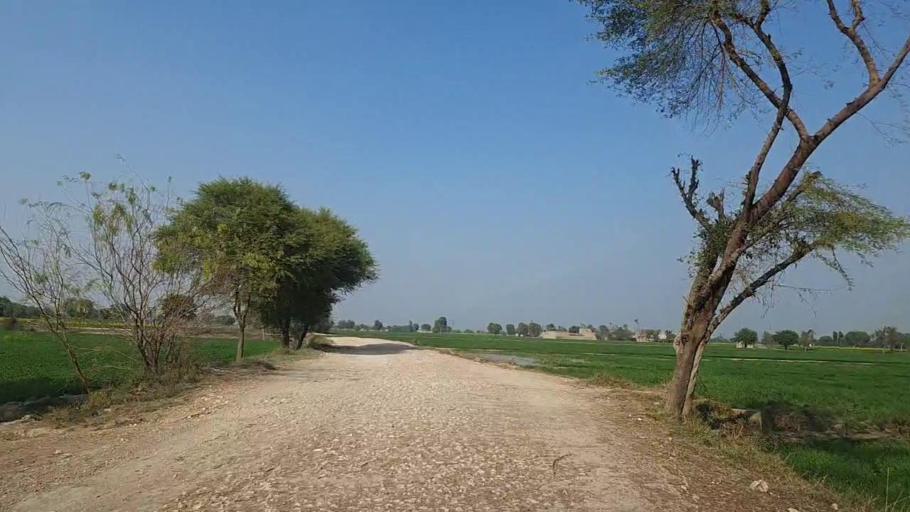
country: PK
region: Sindh
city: Moro
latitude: 26.6969
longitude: 67.9519
